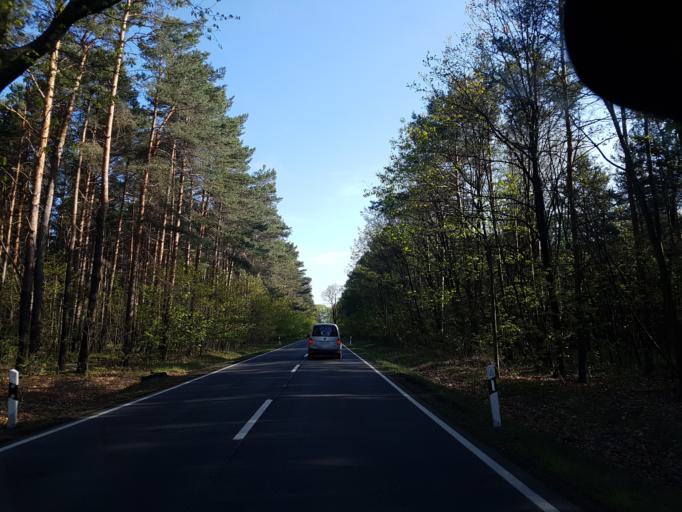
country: DE
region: Brandenburg
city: Grossraschen
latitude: 51.6067
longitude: 14.0189
